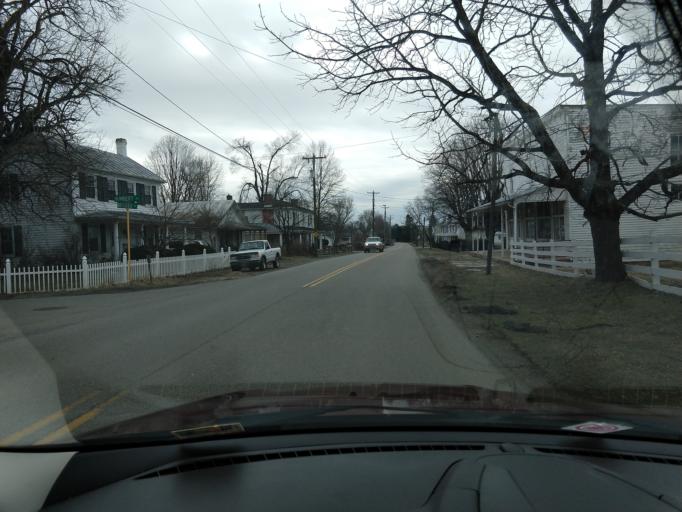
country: US
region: Virginia
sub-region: Augusta County
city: Crimora
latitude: 38.1979
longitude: -78.9058
